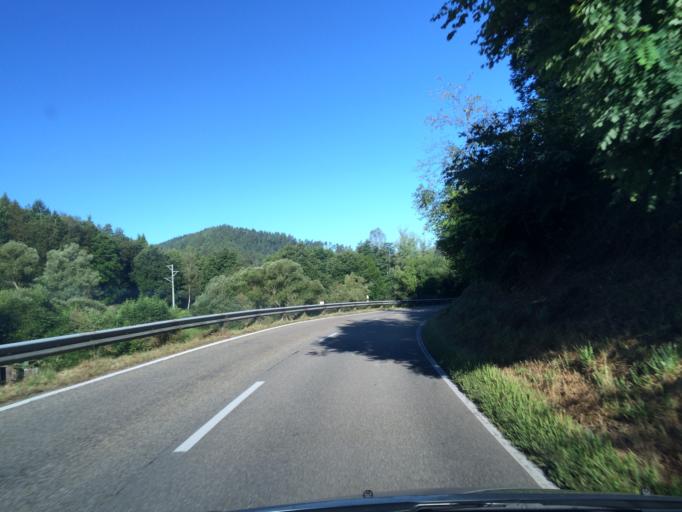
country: DE
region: Rheinland-Pfalz
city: Niederschlettenbach
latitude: 49.0859
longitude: 7.8383
